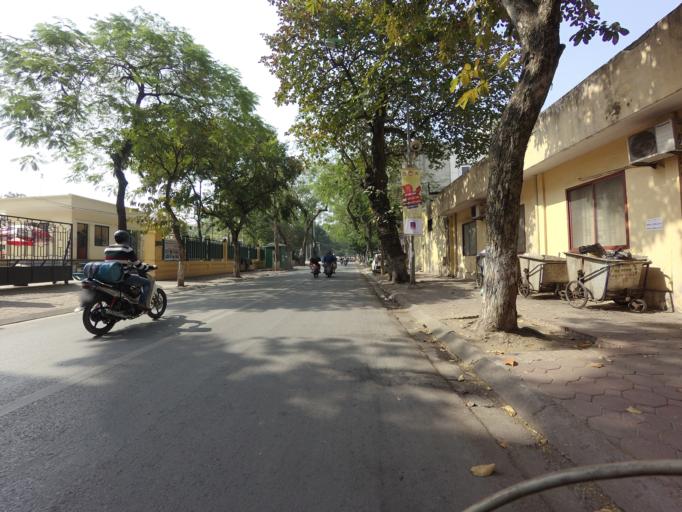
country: VN
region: Ha Noi
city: Hanoi
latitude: 21.0428
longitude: 105.8372
